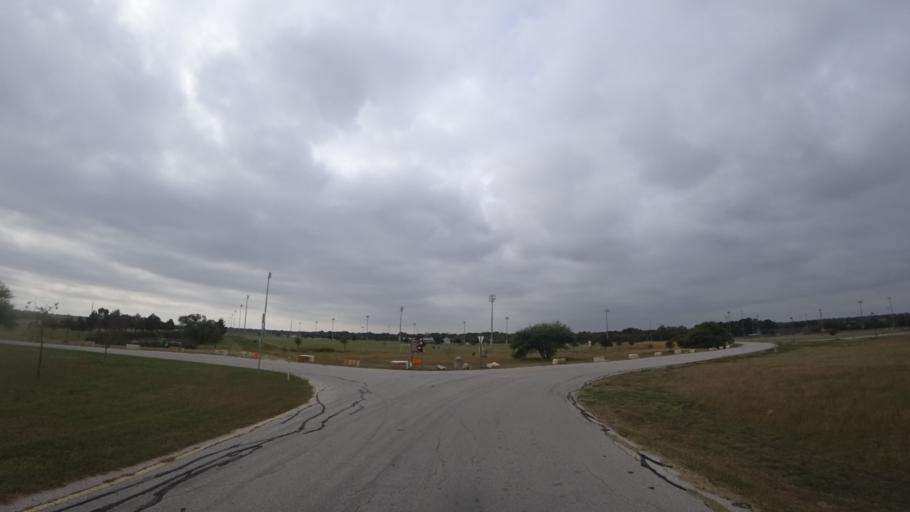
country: US
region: Texas
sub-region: Travis County
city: Pflugerville
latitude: 30.4154
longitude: -97.5954
